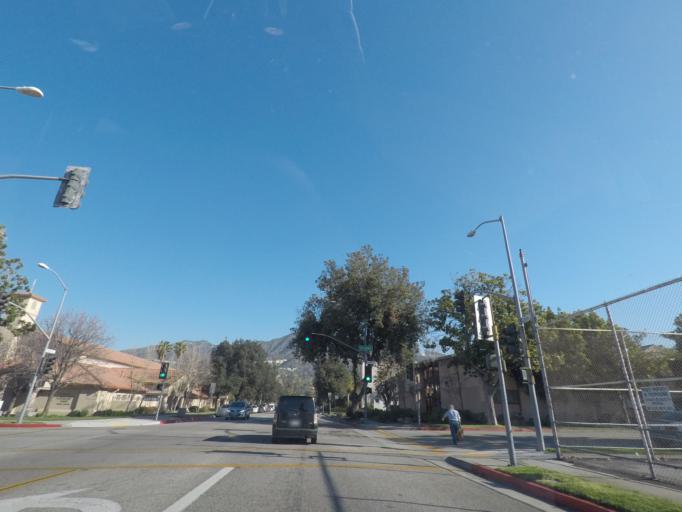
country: US
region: California
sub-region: Los Angeles County
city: North Glendale
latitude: 34.1613
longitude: -118.2568
